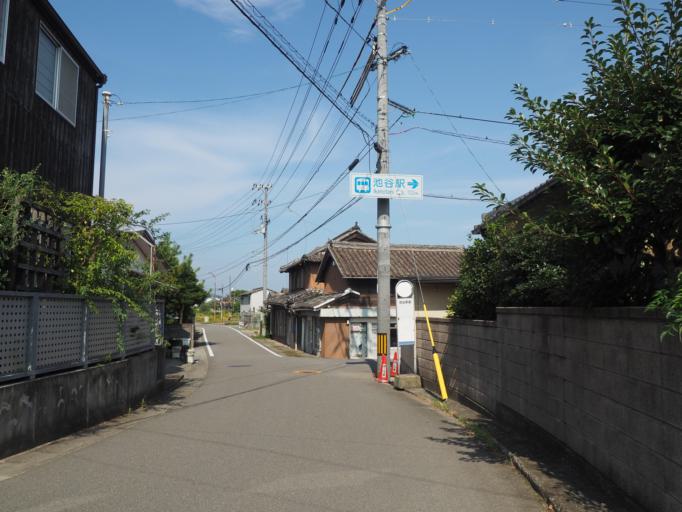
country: JP
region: Tokushima
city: Narutocho-mitsuishi
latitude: 34.1537
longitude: 134.5285
